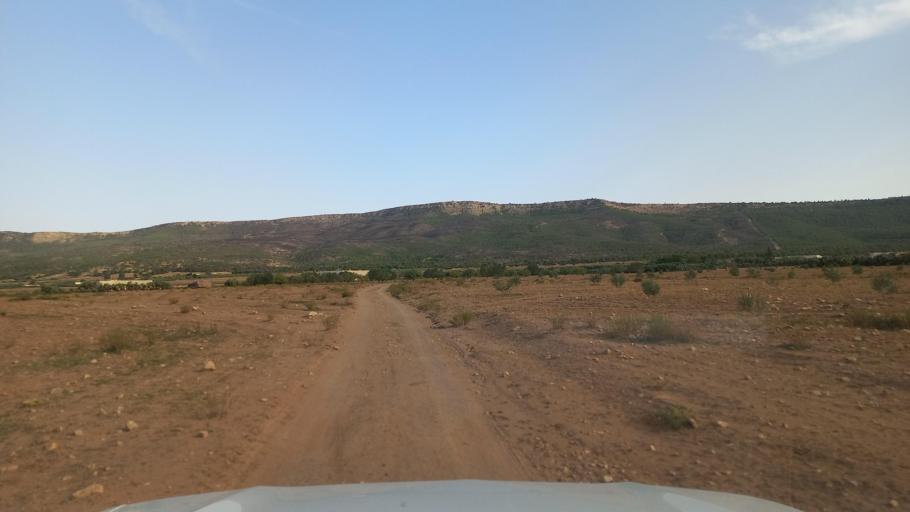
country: TN
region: Al Qasrayn
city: Kasserine
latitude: 35.3549
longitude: 8.8544
